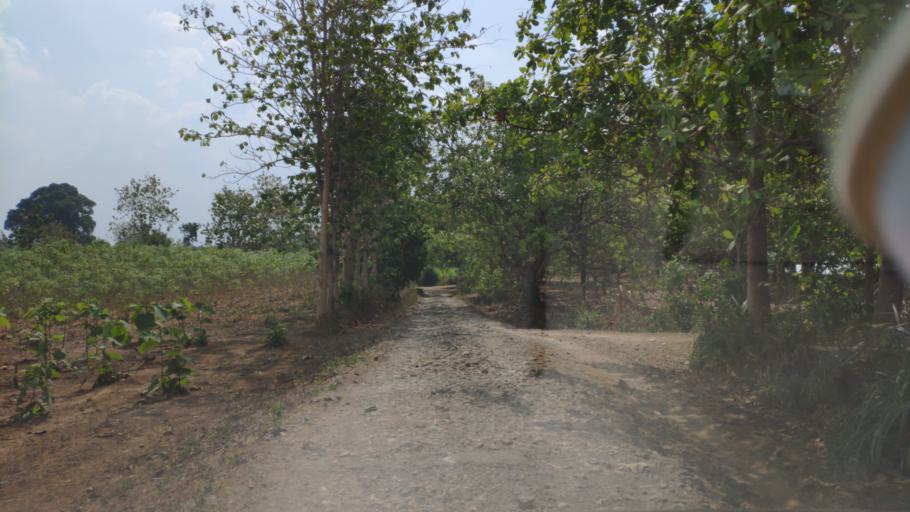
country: ID
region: Central Java
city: Krocok
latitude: -6.9710
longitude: 111.2651
